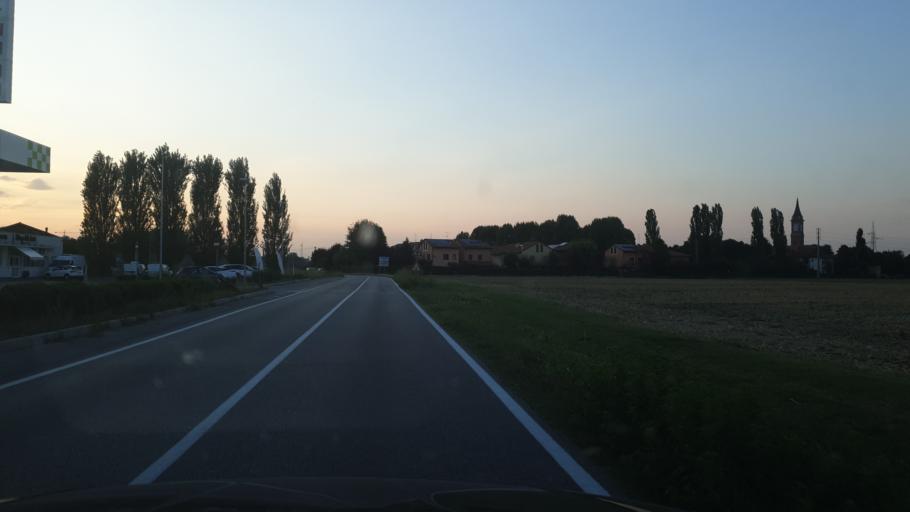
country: IT
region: Emilia-Romagna
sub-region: Provincia di Bologna
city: Progresso
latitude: 44.5678
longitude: 11.3933
